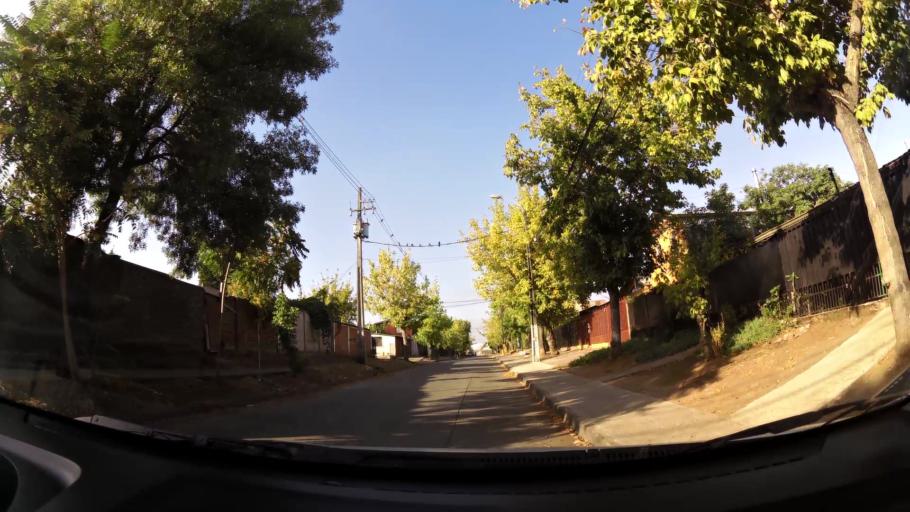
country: CL
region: Maule
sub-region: Provincia de Talca
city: Talca
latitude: -35.4080
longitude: -71.6522
